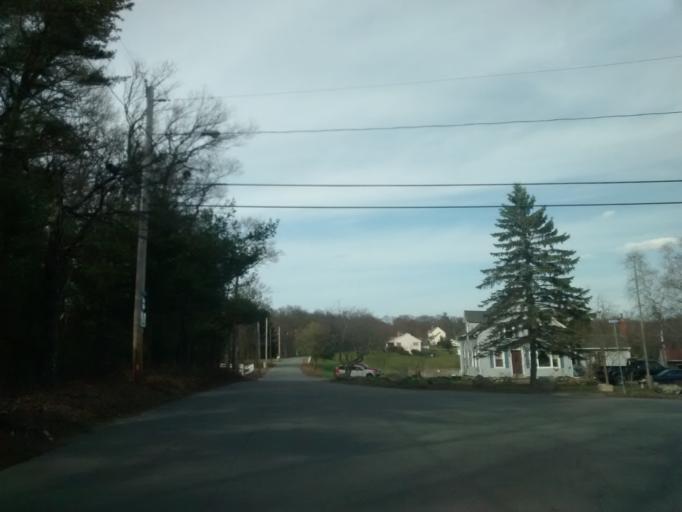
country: US
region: Massachusetts
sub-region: Norfolk County
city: Plainville
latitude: 42.0048
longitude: -71.3675
